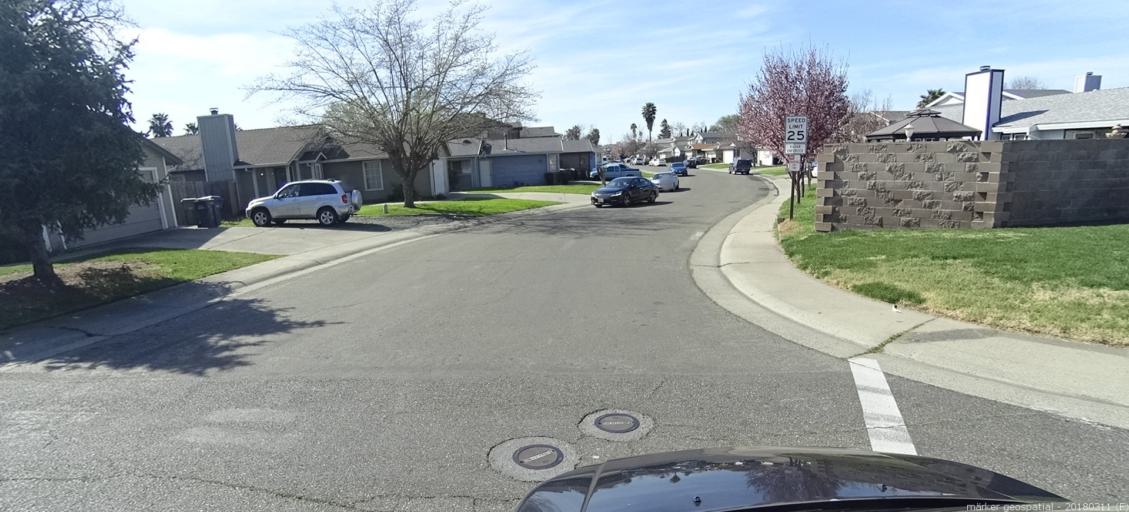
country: US
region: California
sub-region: Sacramento County
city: Florin
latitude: 38.4828
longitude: -121.4273
